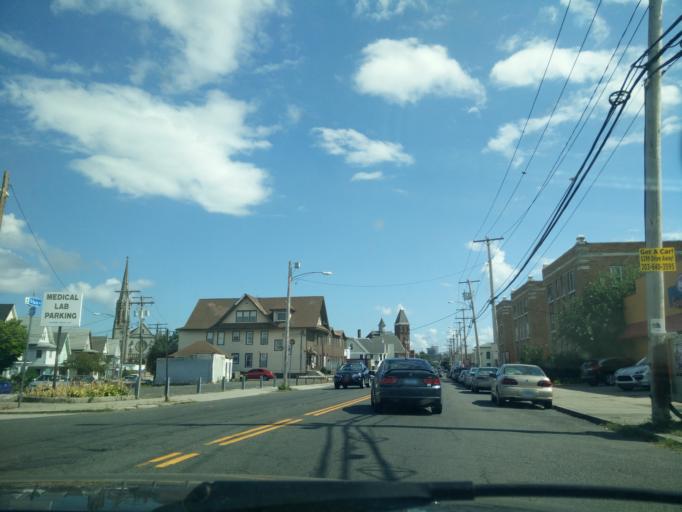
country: US
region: Connecticut
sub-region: Fairfield County
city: Bridgeport
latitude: 41.1939
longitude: -73.1985
